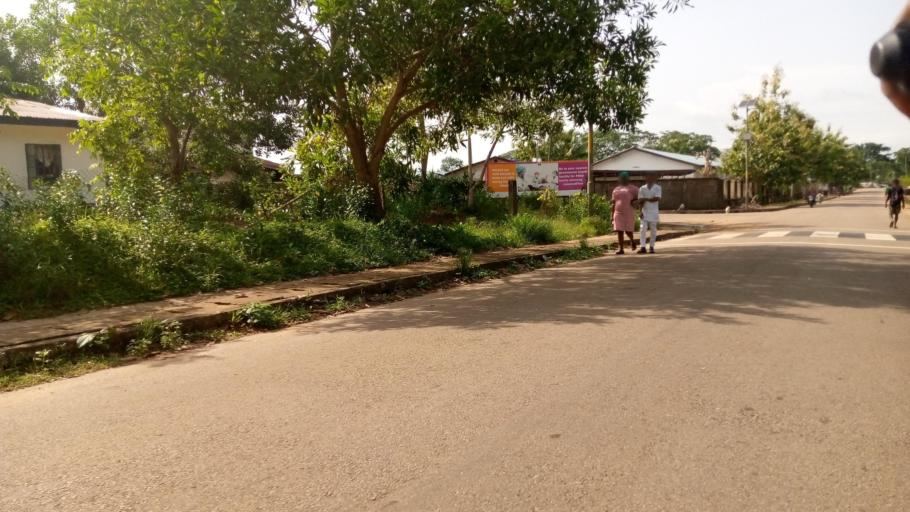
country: SL
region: Southern Province
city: Pujehun
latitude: 7.3516
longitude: -11.7197
